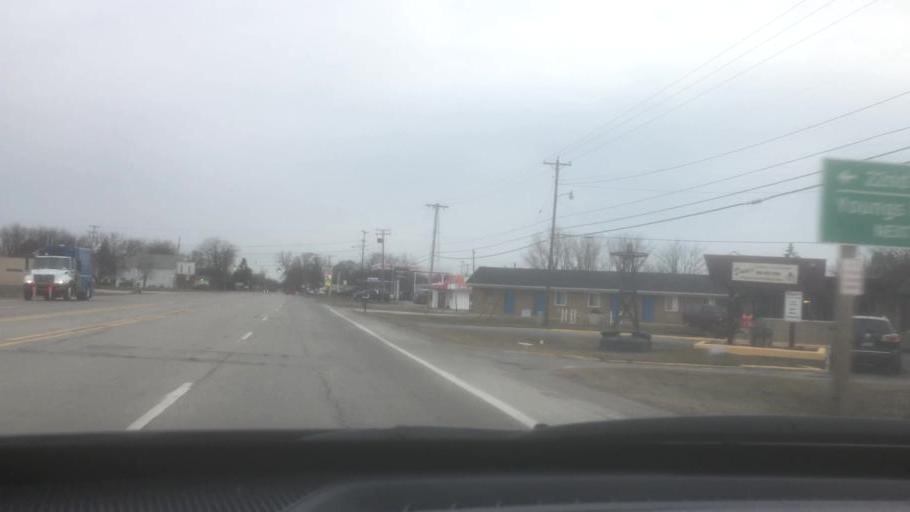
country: US
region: Michigan
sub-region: Bay County
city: Bay City
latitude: 43.5785
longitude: -83.8554
